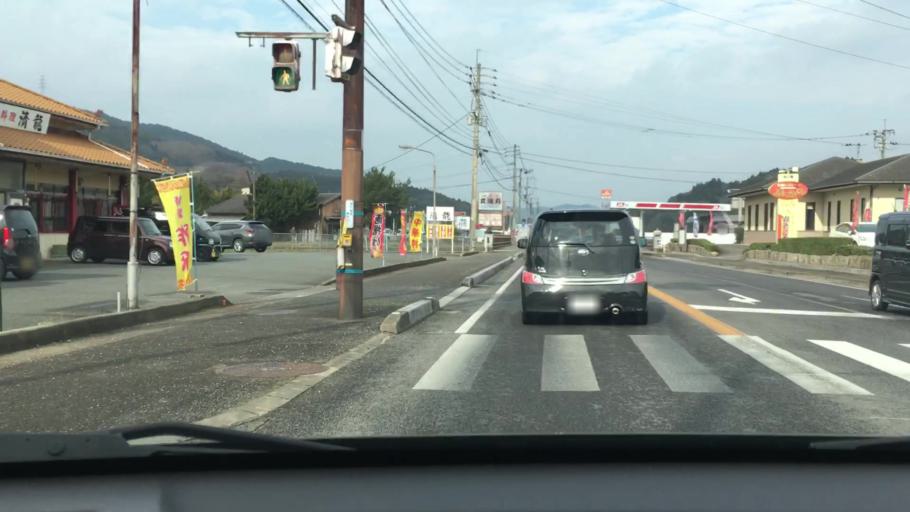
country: JP
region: Saga Prefecture
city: Imaricho-ko
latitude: 33.3136
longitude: 129.9286
